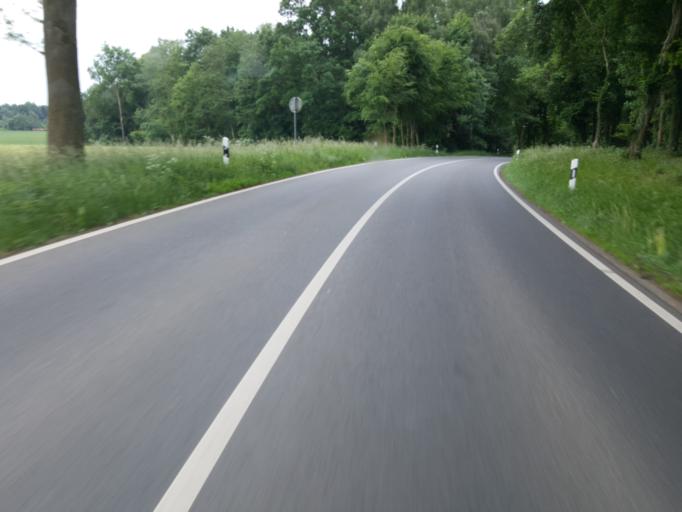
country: DE
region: Lower Saxony
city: Rehburg-Loccum
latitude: 52.4471
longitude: 9.2181
